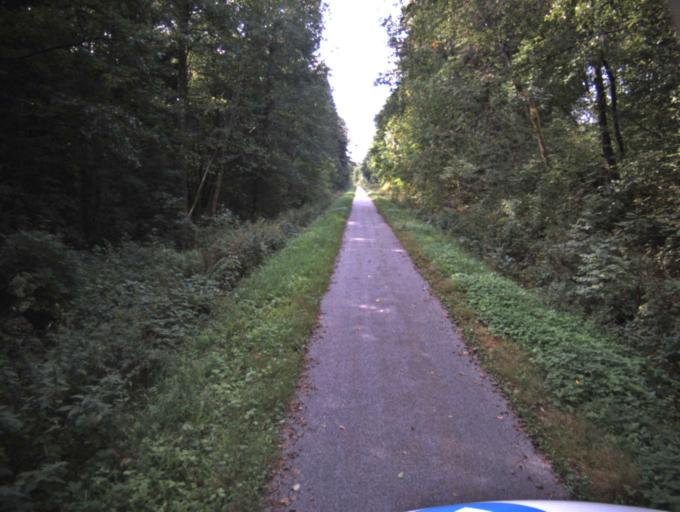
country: SE
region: Vaestra Goetaland
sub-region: Tranemo Kommun
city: Limmared
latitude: 57.6641
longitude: 13.3645
